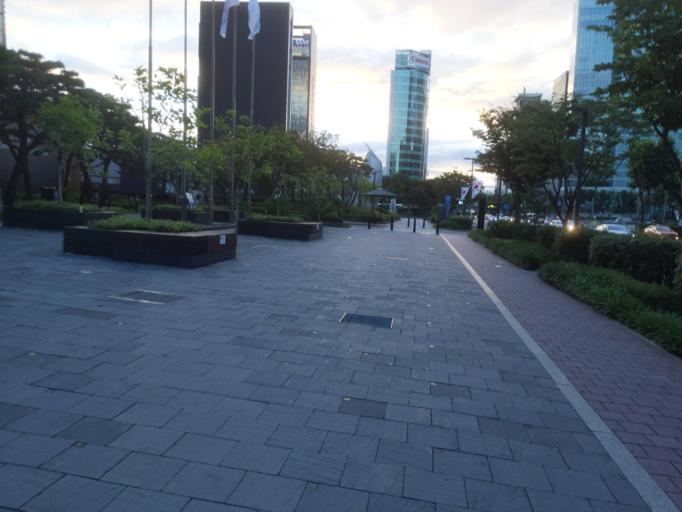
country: KR
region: Seoul
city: Seoul
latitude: 37.5084
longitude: 127.0611
